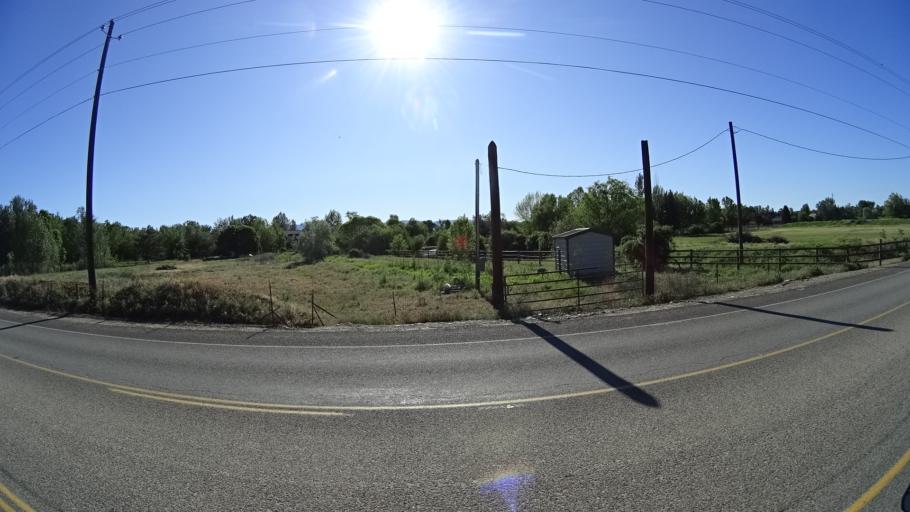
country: US
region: Idaho
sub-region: Ada County
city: Eagle
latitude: 43.6858
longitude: -116.4139
